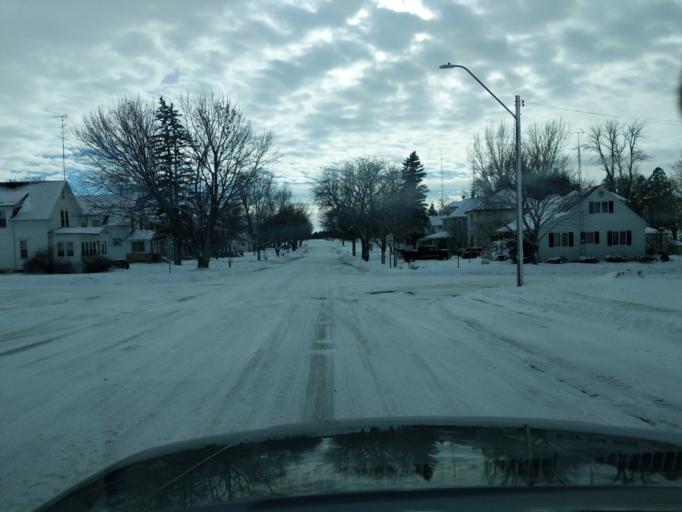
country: US
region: Minnesota
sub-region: Renville County
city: Renville
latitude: 44.7861
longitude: -95.3516
